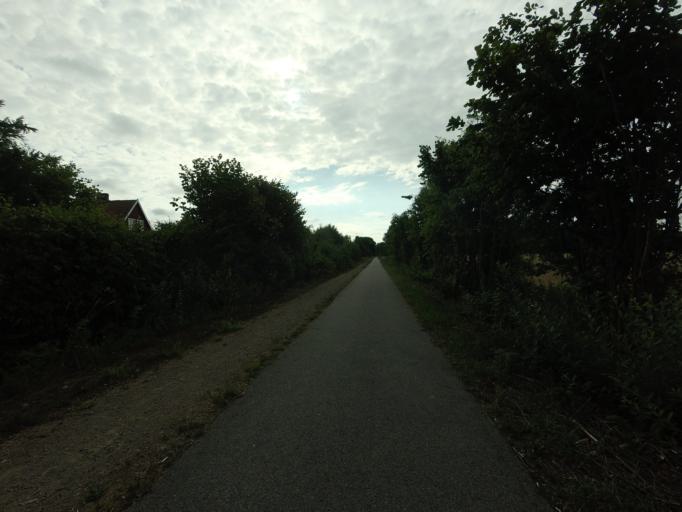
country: SE
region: Skane
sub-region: Helsingborg
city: Odakra
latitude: 56.1743
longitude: 12.6923
